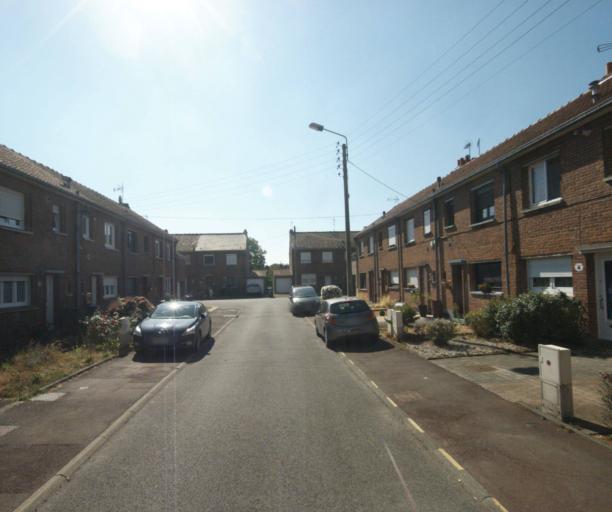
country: FR
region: Nord-Pas-de-Calais
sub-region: Departement du Nord
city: Bousbecque
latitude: 50.7690
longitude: 3.0690
